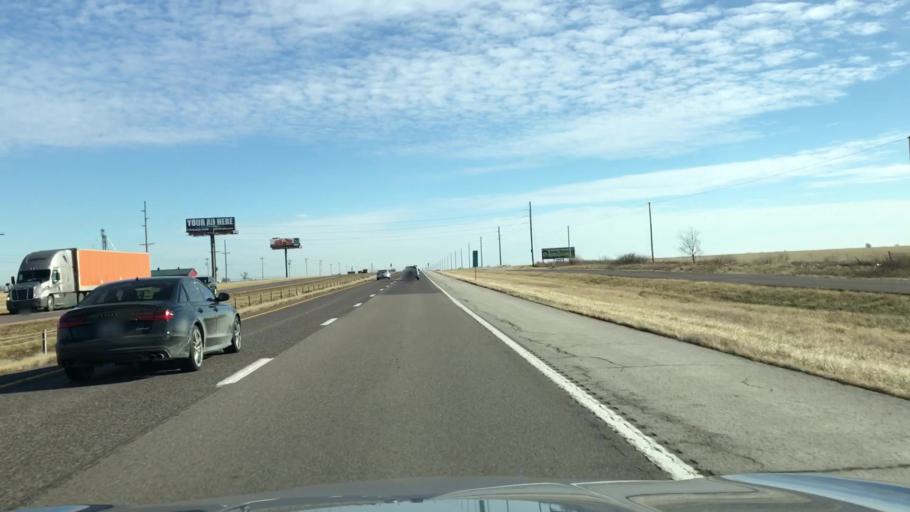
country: US
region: Missouri
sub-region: Callaway County
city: Fulton
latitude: 38.9528
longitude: -92.0819
